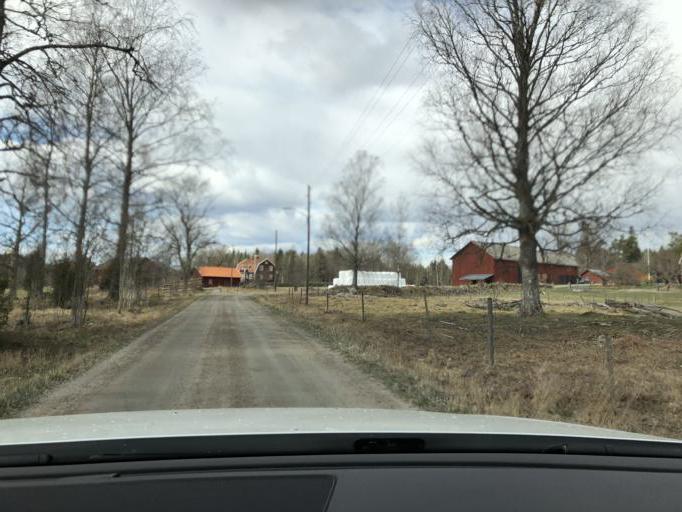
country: SE
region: Gaevleborg
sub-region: Gavle Kommun
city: Hedesunda
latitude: 60.3142
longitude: 17.1073
